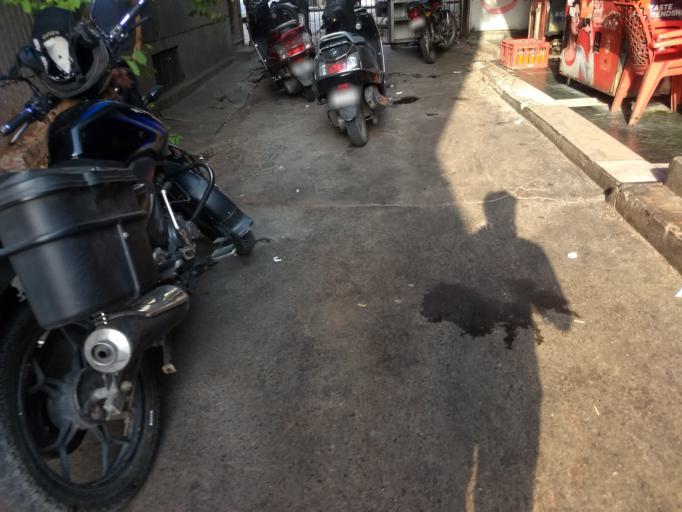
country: IN
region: NCT
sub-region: New Delhi
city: New Delhi
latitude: 28.5660
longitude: 77.2465
